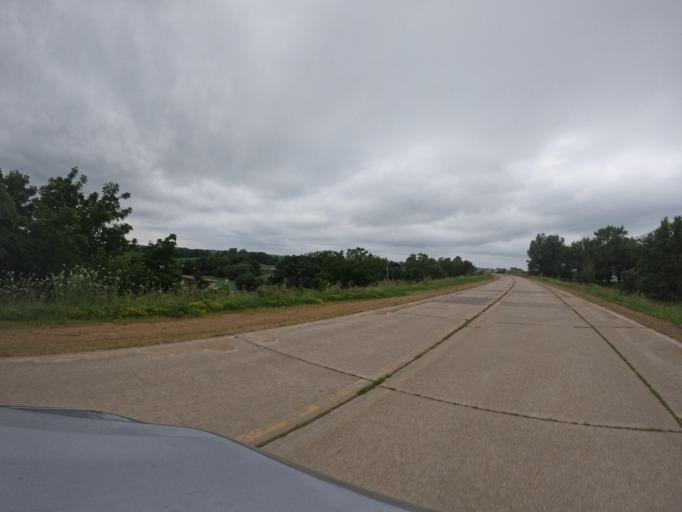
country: US
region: Iowa
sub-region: Jackson County
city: Maquoketa
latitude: 41.9472
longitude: -90.6234
